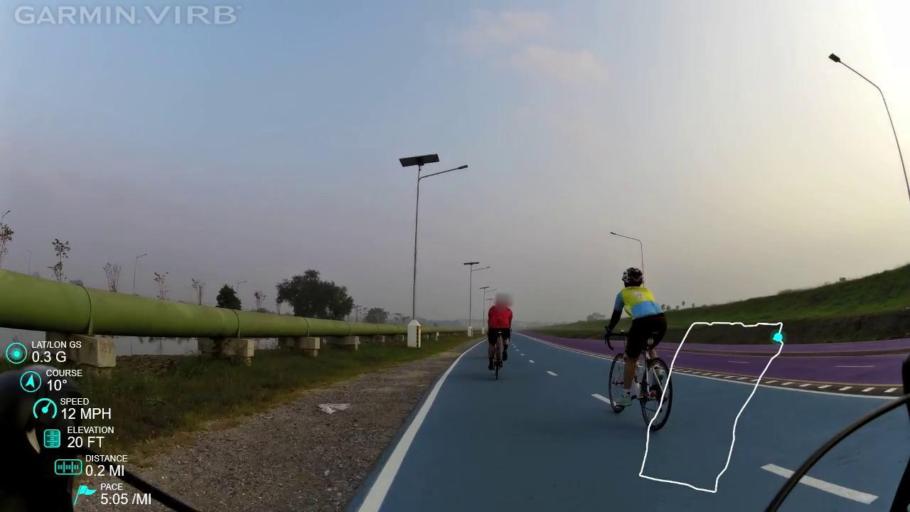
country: TH
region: Bangkok
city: Lat Krabang
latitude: 13.6989
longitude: 100.7762
